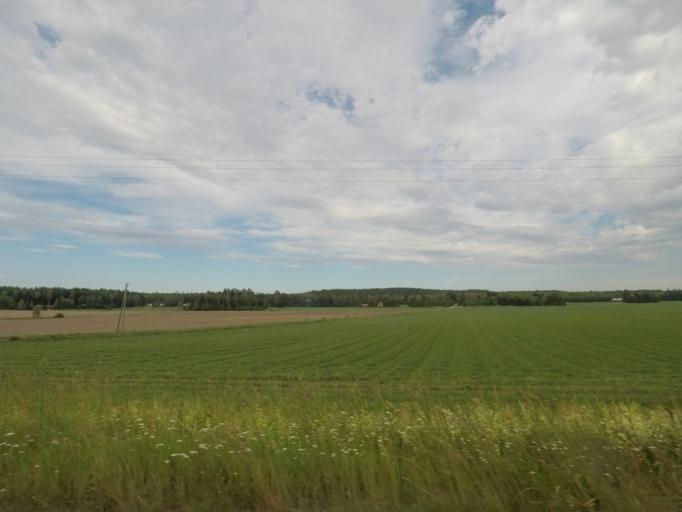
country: FI
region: Paijanne Tavastia
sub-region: Lahti
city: Hollola
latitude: 60.8573
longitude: 25.4996
